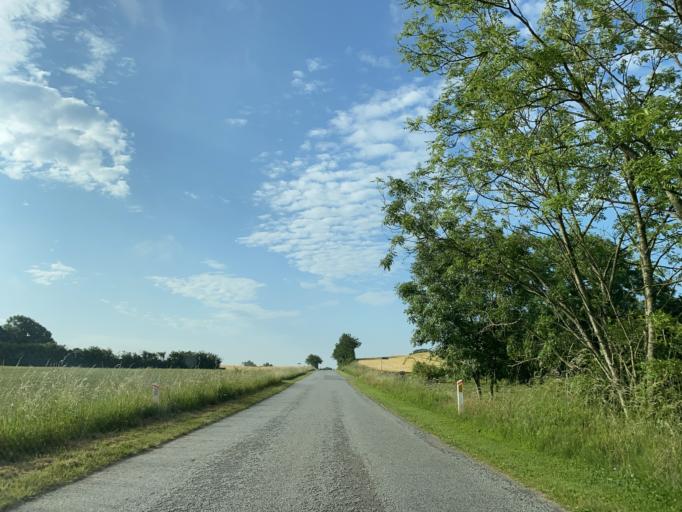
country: DK
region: South Denmark
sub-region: Haderslev Kommune
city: Haderslev
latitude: 55.1832
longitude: 9.4795
